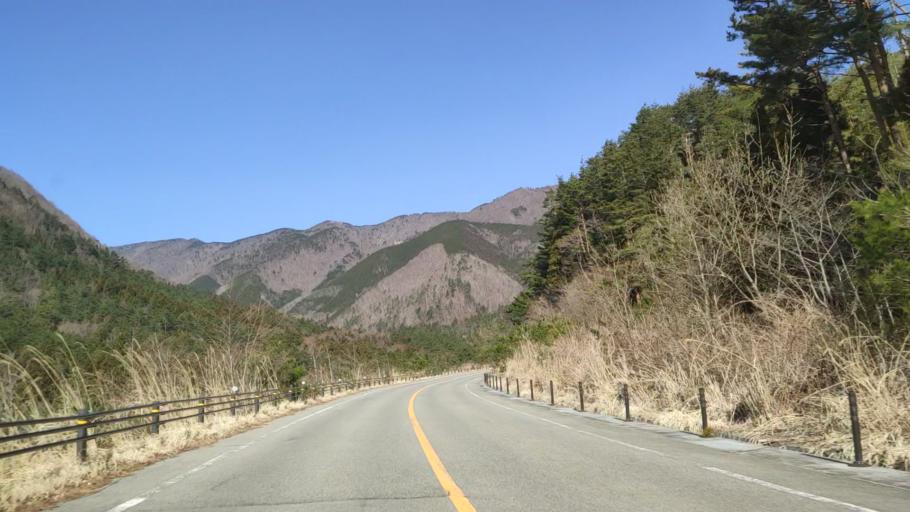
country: JP
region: Yamanashi
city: Fujikawaguchiko
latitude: 35.5255
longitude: 138.7210
